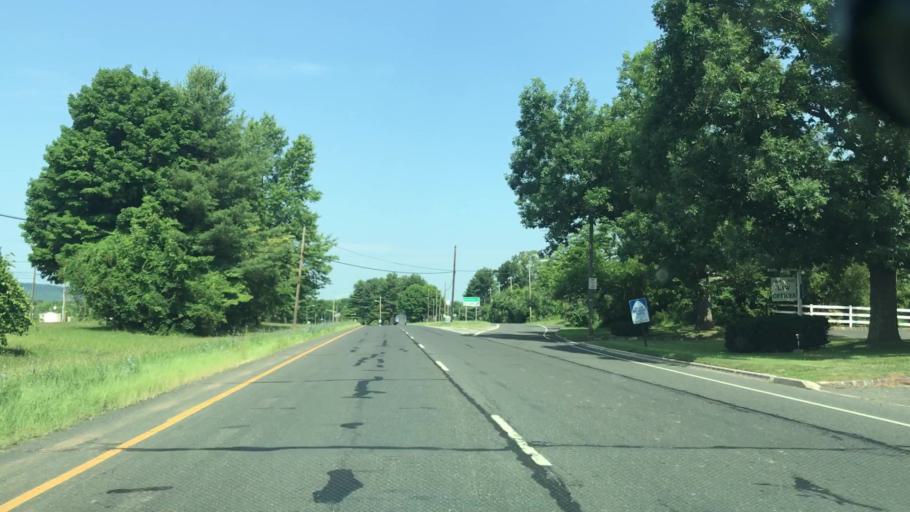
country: US
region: New Jersey
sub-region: Hunterdon County
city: Whitehouse Station
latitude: 40.6156
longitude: -74.7375
